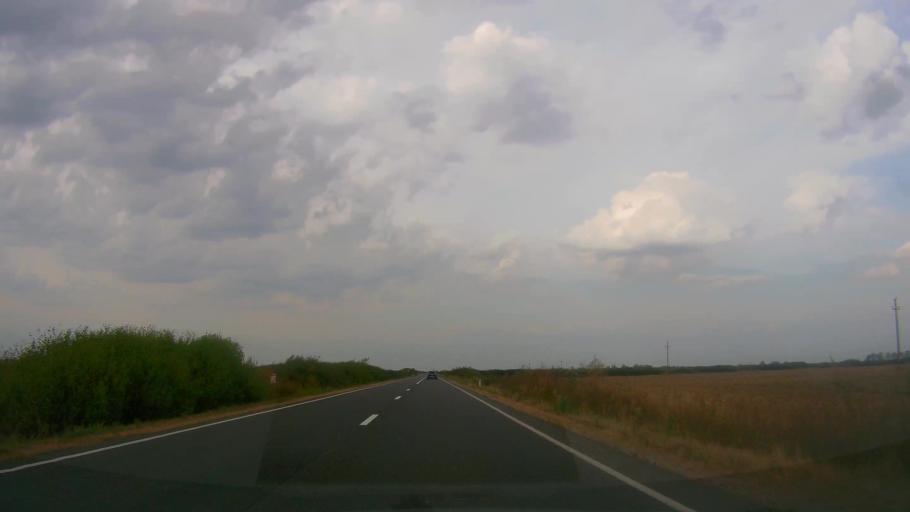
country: RO
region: Satu Mare
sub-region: Comuna Acas
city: Acas
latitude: 47.5396
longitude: 22.8108
